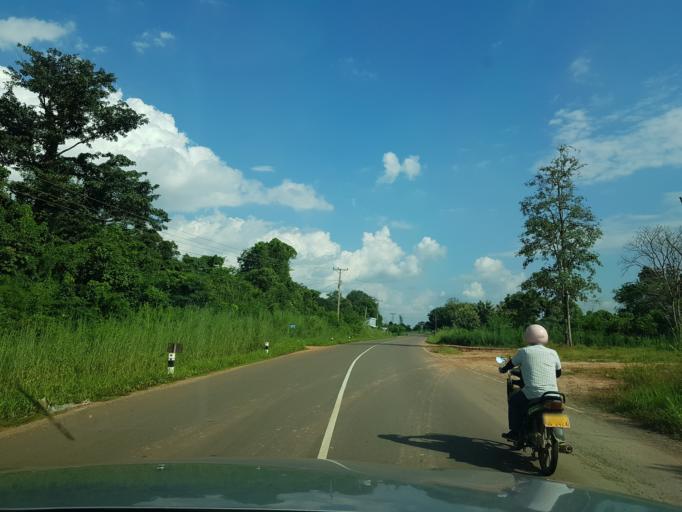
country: TH
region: Nong Khai
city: Pho Tak
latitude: 17.9851
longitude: 102.4407
